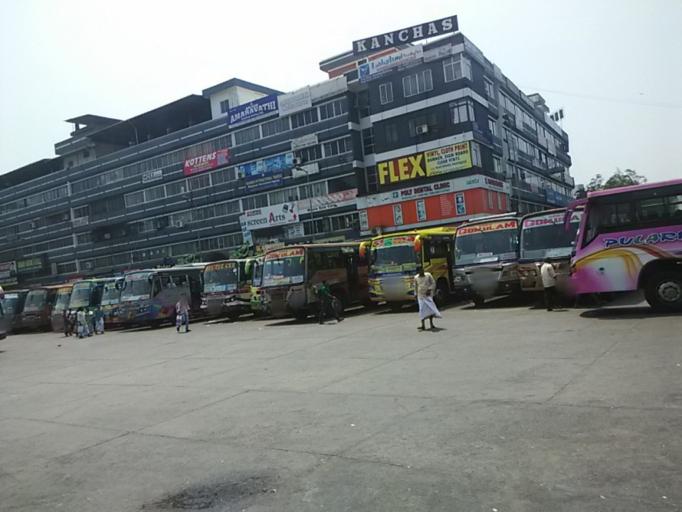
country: IN
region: Kerala
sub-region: Kozhikode
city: Kozhikode
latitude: 11.2580
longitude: 75.7865
